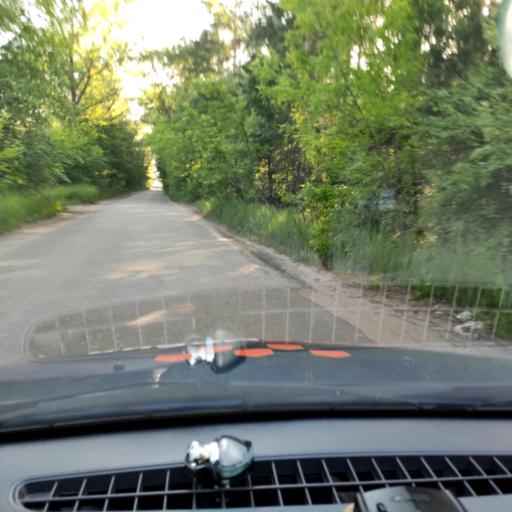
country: RU
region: Voronezj
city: Ramon'
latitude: 51.8482
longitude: 39.2306
